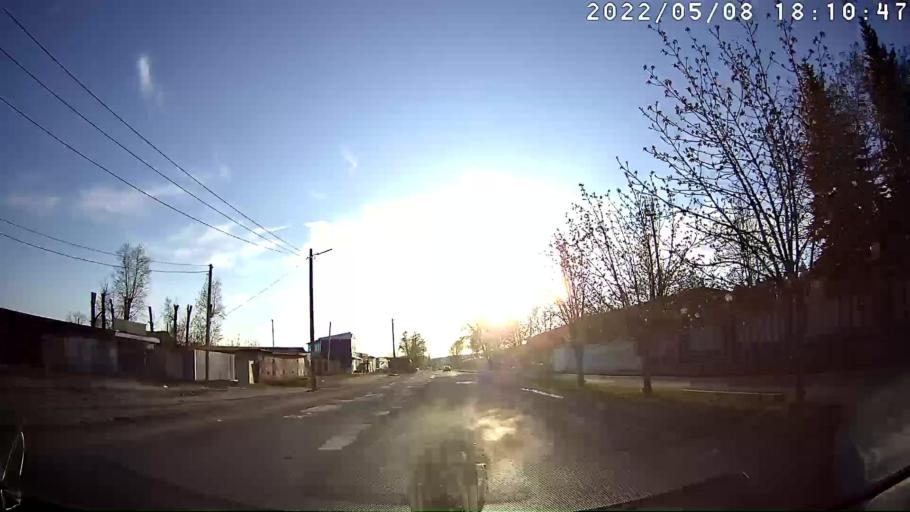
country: RU
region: Tatarstan
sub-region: Zelenodol'skiy Rayon
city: Zelenodolsk
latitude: 55.8396
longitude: 48.5202
